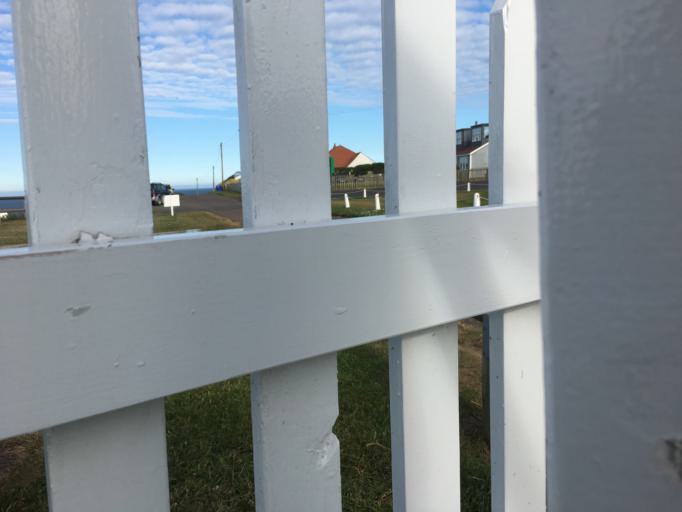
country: GB
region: England
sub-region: Northumberland
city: Bamburgh
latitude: 55.6164
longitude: -1.7281
